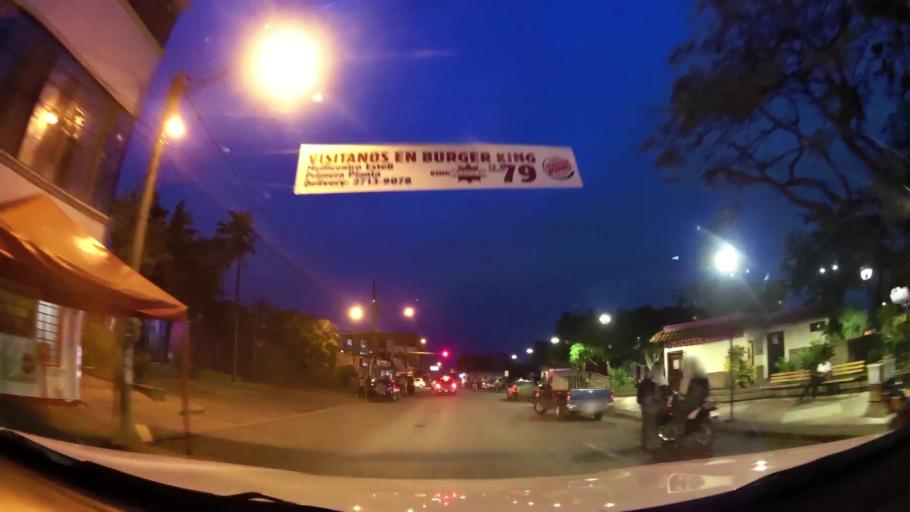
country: NI
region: Esteli
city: Esteli
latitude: 13.0927
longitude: -86.3567
